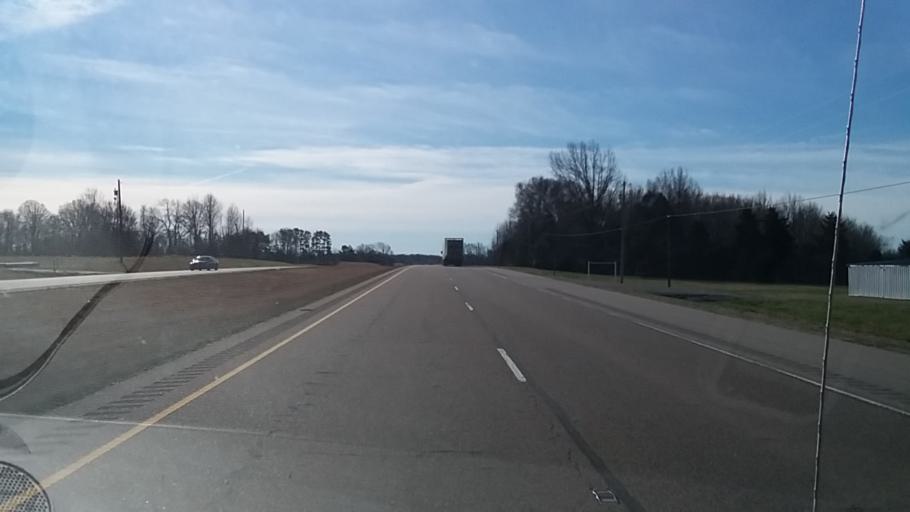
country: US
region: Tennessee
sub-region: Crockett County
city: Alamo
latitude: 35.8615
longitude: -89.2066
